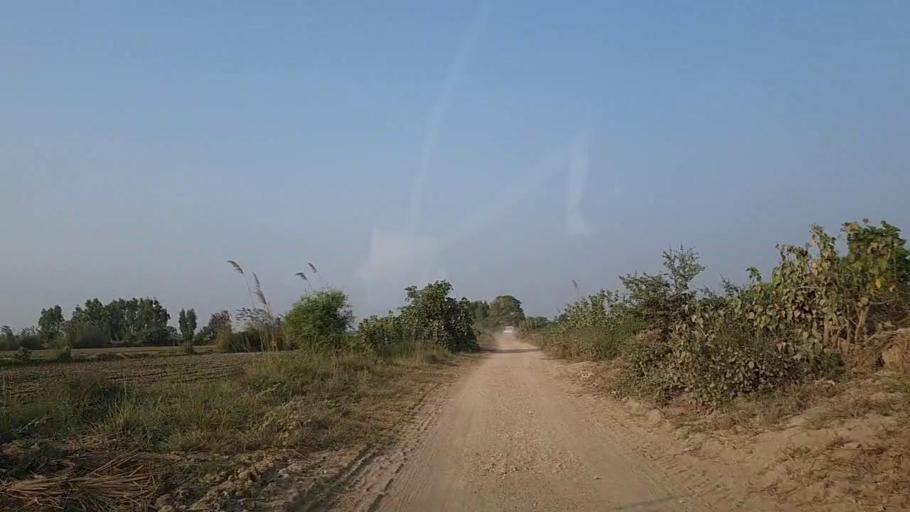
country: PK
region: Sindh
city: Thatta
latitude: 24.6785
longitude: 67.7843
